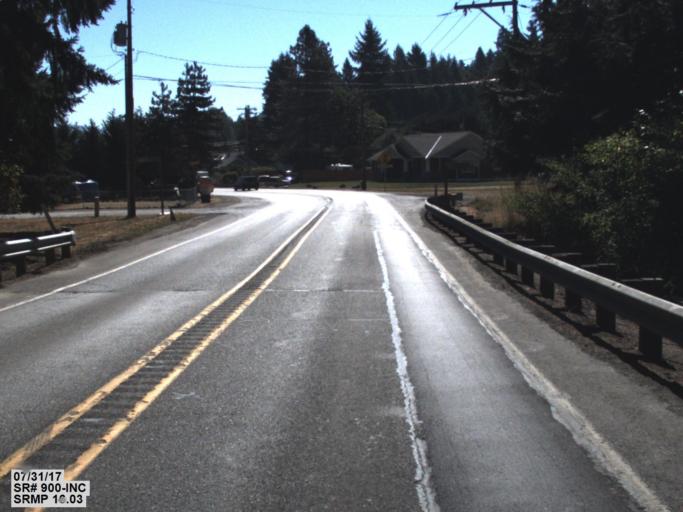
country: US
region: Washington
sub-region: King County
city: East Renton Highlands
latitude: 47.5010
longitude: -122.1252
